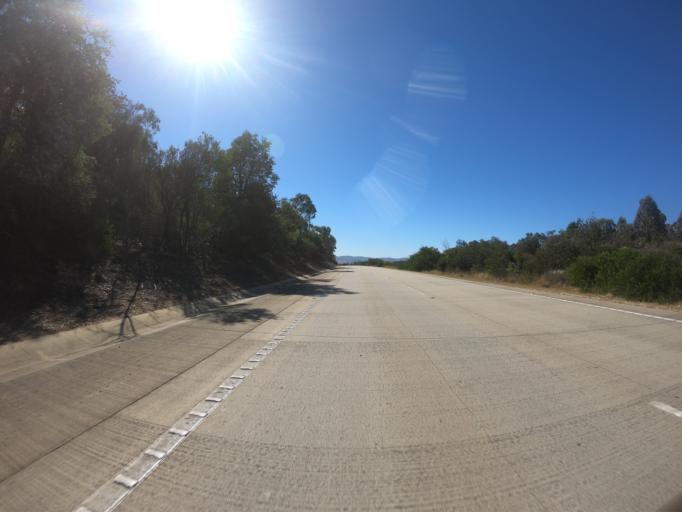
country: AU
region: New South Wales
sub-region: Yass Valley
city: Gundaroo
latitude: -35.1070
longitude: 149.3709
